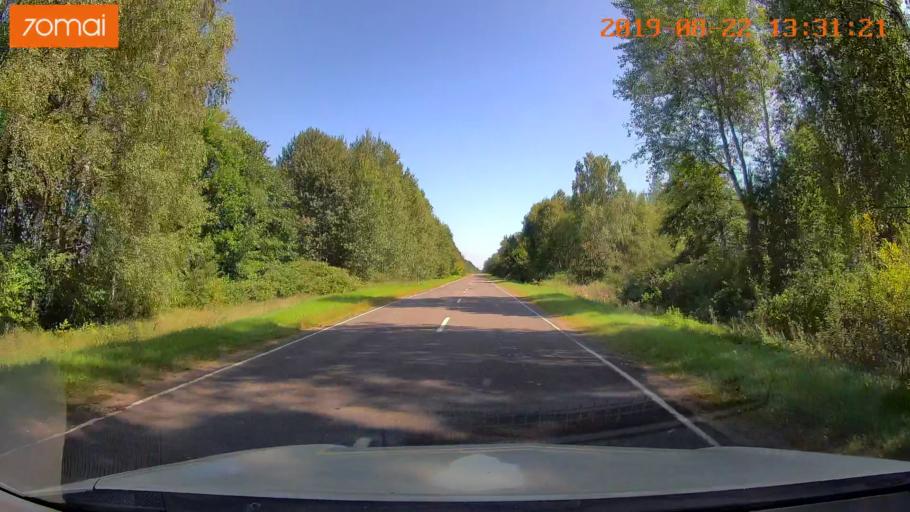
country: BY
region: Minsk
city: Staryya Darohi
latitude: 53.2173
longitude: 28.1773
